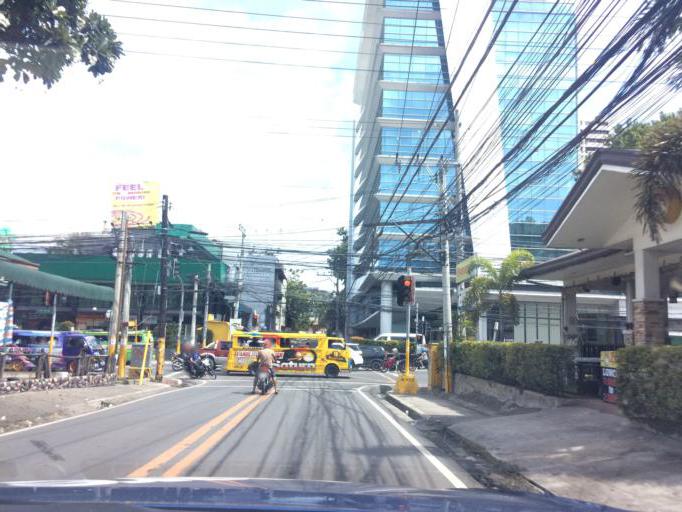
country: PH
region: Central Visayas
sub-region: Province of Cebu
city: Cebu City
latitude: 10.3166
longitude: 123.8934
